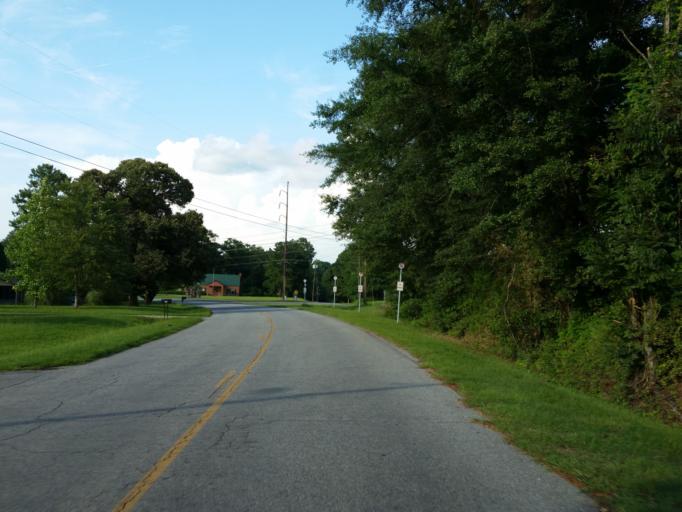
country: US
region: Georgia
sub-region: Dooly County
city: Vienna
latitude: 32.0848
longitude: -83.8004
